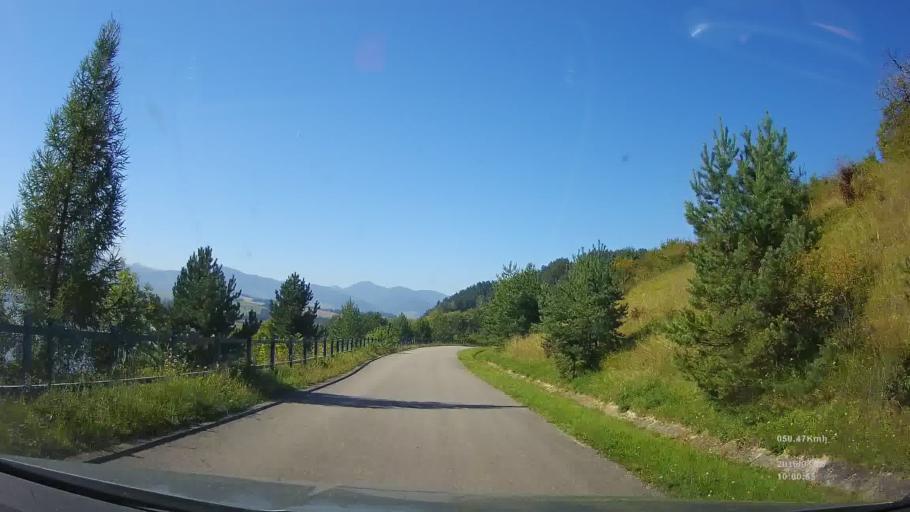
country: SK
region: Zilinsky
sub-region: Okres Liptovsky Mikulas
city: Liptovsky Mikulas
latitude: 49.1075
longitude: 19.4900
